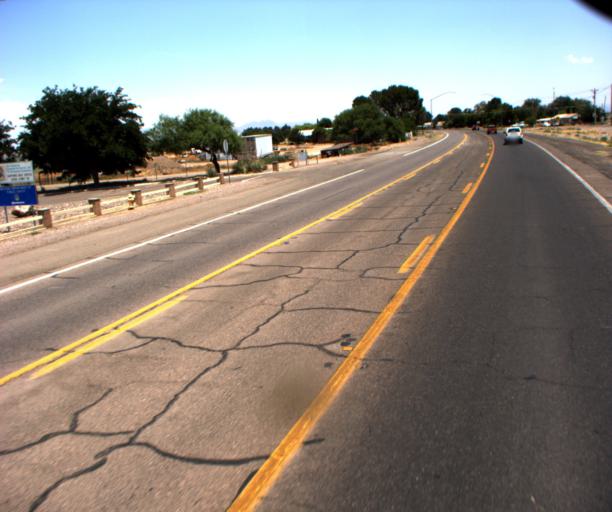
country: US
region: Arizona
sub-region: Graham County
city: Safford
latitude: 32.8175
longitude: -109.6808
